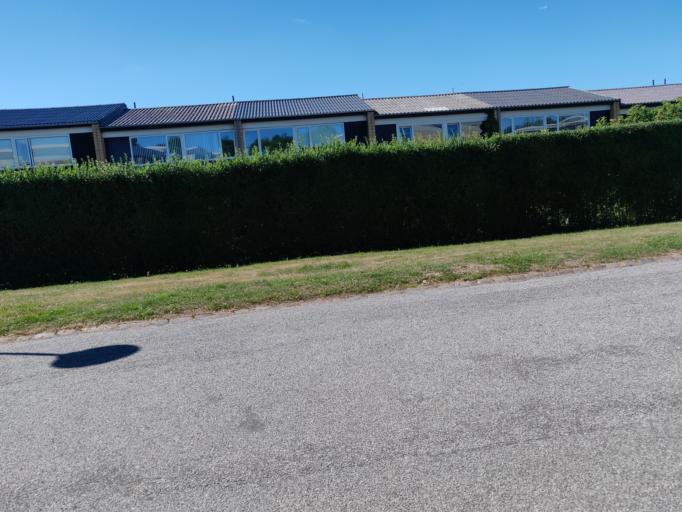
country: DK
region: North Denmark
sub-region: Alborg Kommune
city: Aalborg
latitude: 57.0213
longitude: 9.9325
